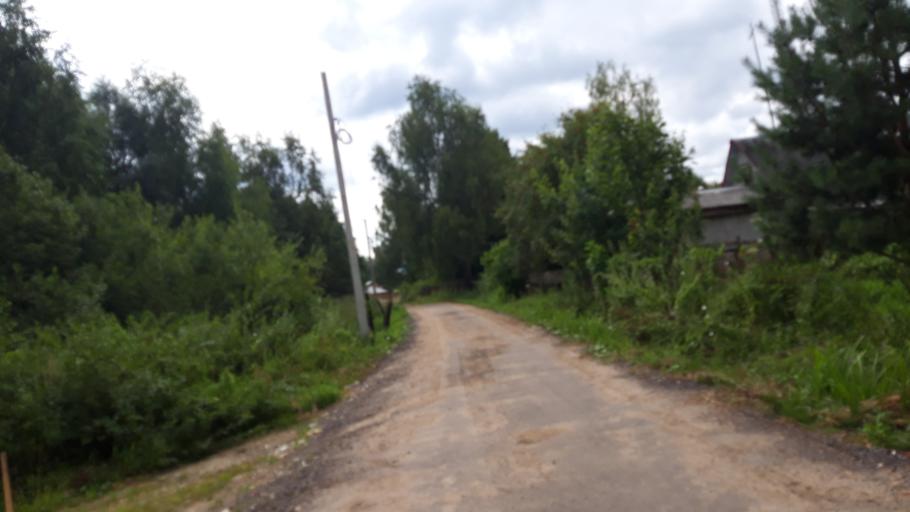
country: RU
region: Tverskaya
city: Konakovo
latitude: 56.6742
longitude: 36.7217
